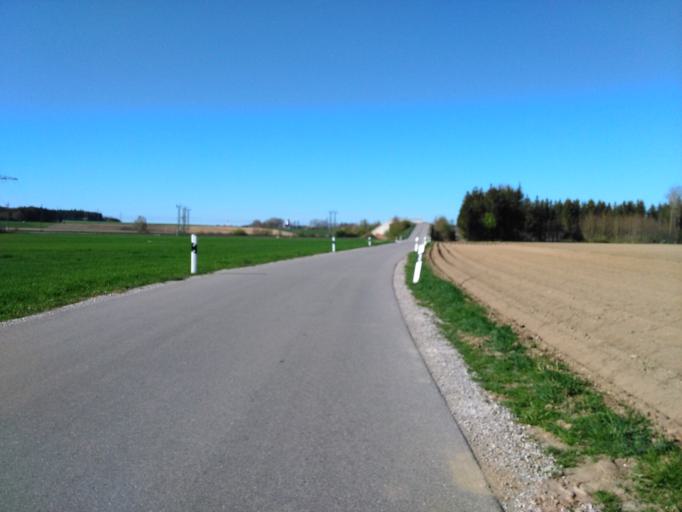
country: DE
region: Bavaria
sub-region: Upper Bavaria
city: Oberschweinbach
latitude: 48.2143
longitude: 11.1904
